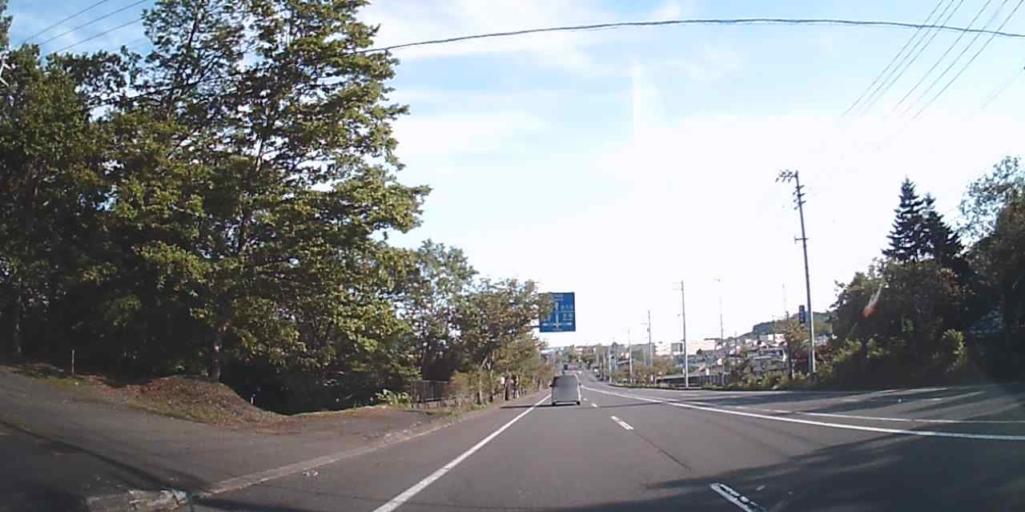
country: JP
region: Hokkaido
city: Shiraoi
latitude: 42.4597
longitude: 141.1777
